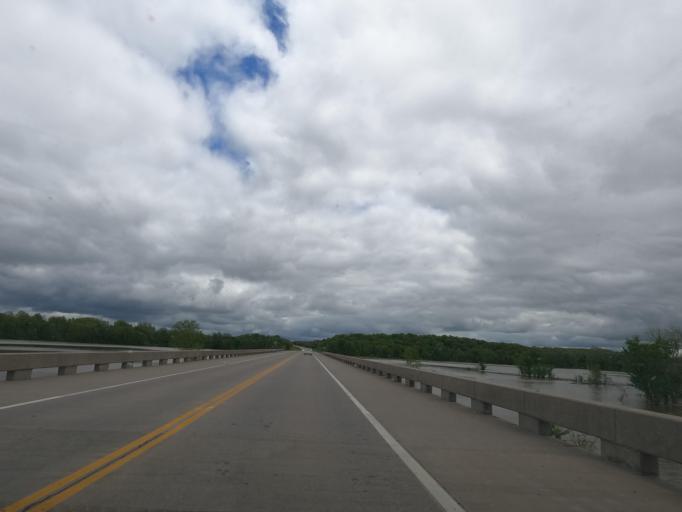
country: US
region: Kansas
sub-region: Wilson County
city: Neodesha
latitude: 37.3567
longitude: -95.6821
